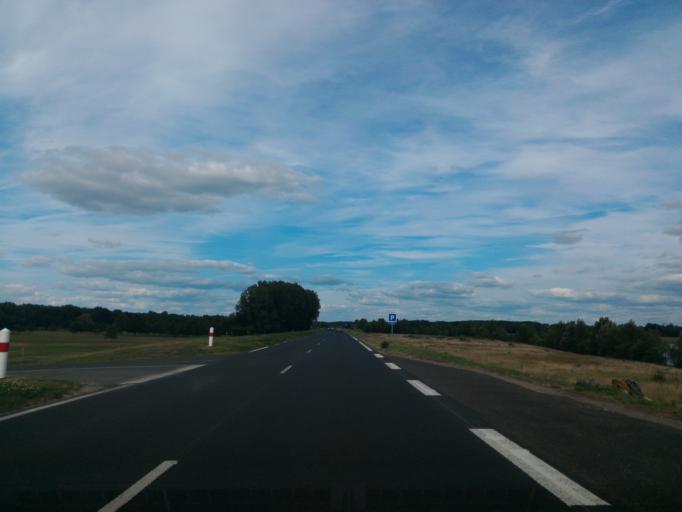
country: FR
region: Centre
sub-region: Departement du Loir-et-Cher
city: Cande-sur-Beuvron
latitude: 47.4980
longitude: 1.2272
